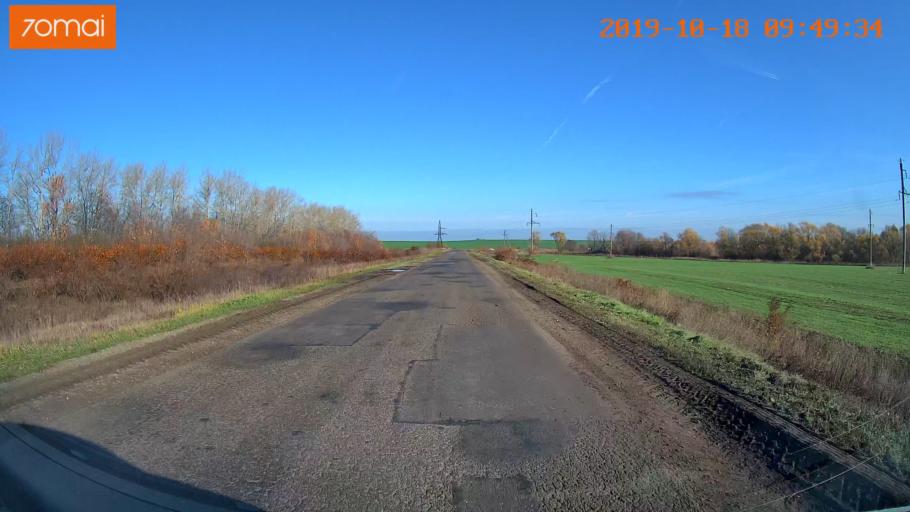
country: RU
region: Tula
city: Kazachka
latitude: 53.3194
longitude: 38.2684
